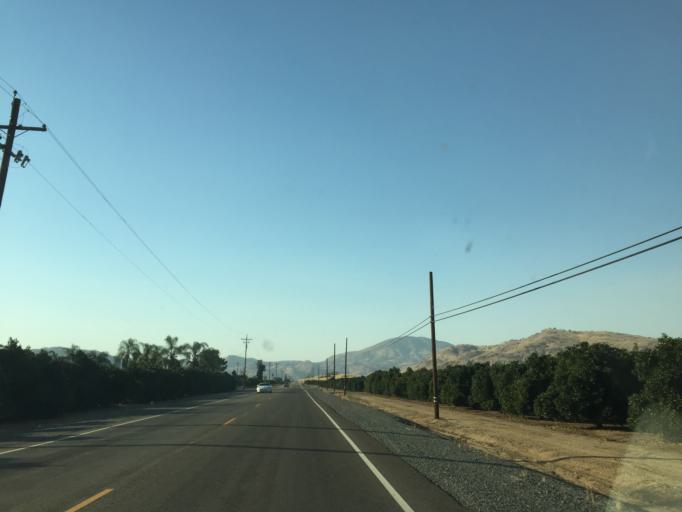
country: US
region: California
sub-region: Fresno County
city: Orange Cove
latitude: 36.6517
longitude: -119.3047
